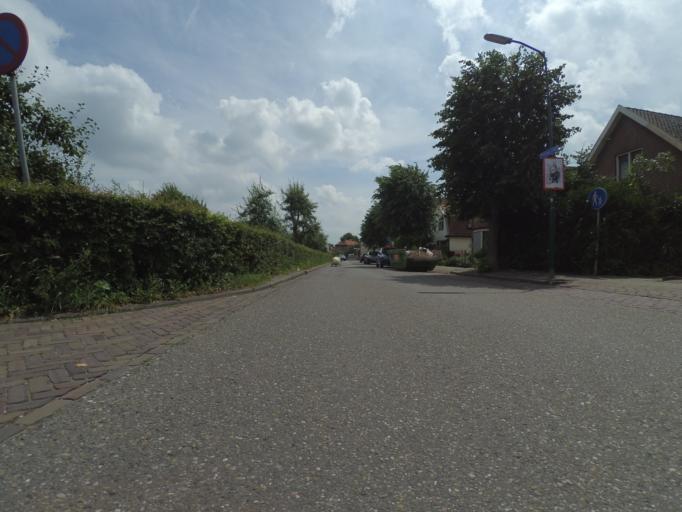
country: NL
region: Utrecht
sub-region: Gemeente Wijk bij Duurstede
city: Wijk bij Duurstede
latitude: 51.9981
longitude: 5.3118
